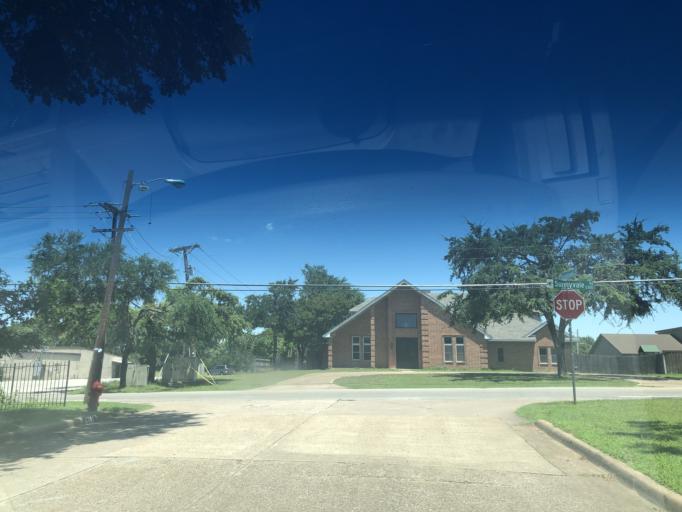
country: US
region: Texas
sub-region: Dallas County
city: Grand Prairie
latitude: 32.7797
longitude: -97.0372
